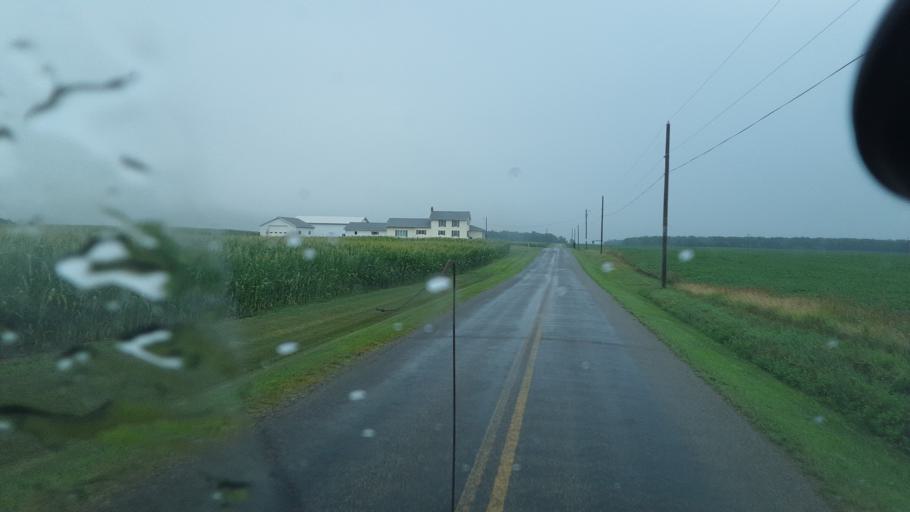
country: US
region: Ohio
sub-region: Williams County
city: Edgerton
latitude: 41.5168
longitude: -84.7879
